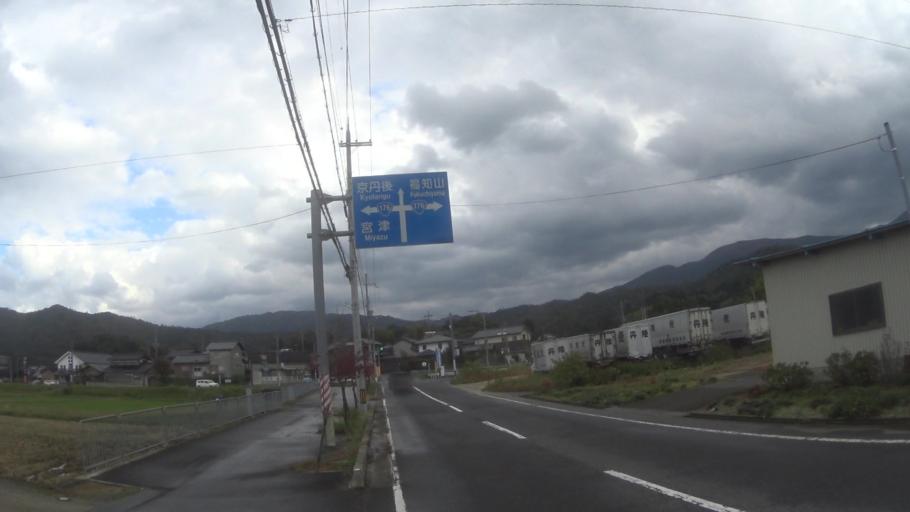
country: JP
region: Kyoto
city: Miyazu
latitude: 35.5112
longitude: 135.1043
